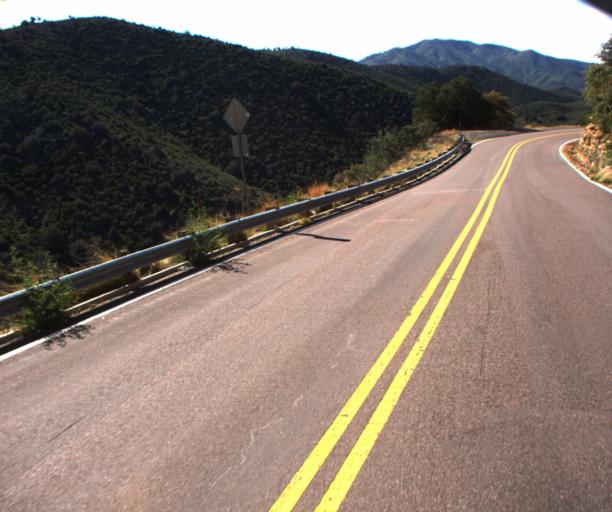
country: US
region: Arizona
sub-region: Yavapai County
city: Prescott
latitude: 34.4671
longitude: -112.5150
